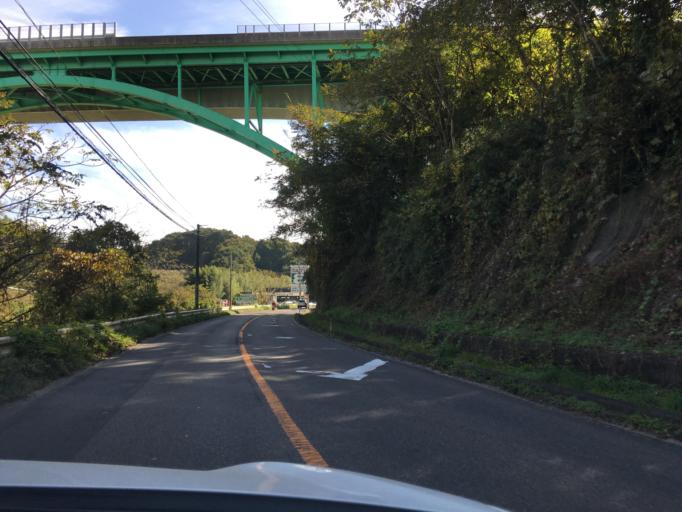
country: JP
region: Fukushima
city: Miharu
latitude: 37.4369
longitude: 140.4667
